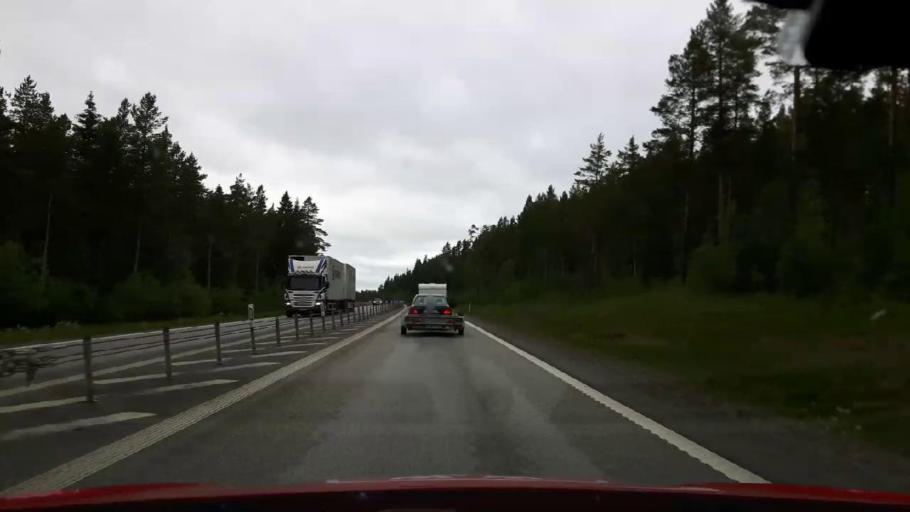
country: SE
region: Jaemtland
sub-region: OEstersunds Kommun
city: Ostersund
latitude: 63.1978
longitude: 14.6853
